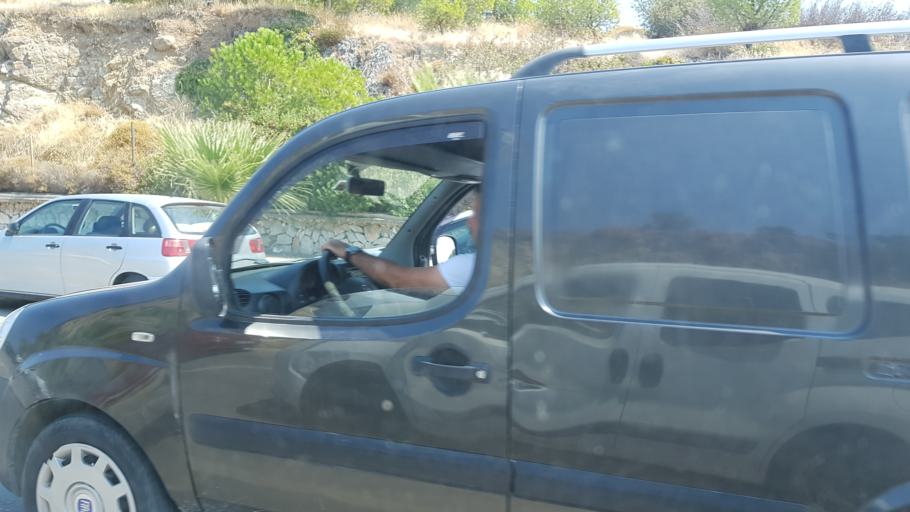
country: TR
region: Izmir
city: Urla
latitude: 38.3780
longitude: 26.7597
